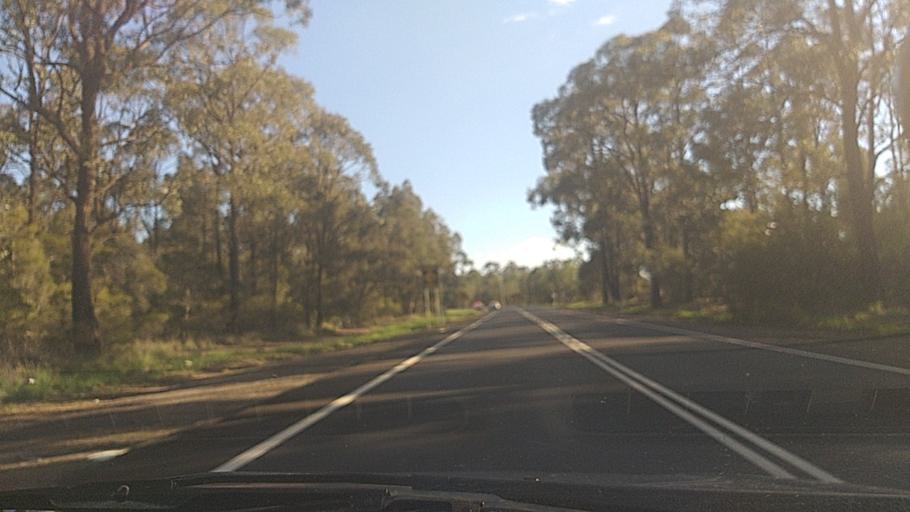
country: AU
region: New South Wales
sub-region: Penrith Municipality
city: Werrington Downs
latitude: -33.7075
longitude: 150.7232
